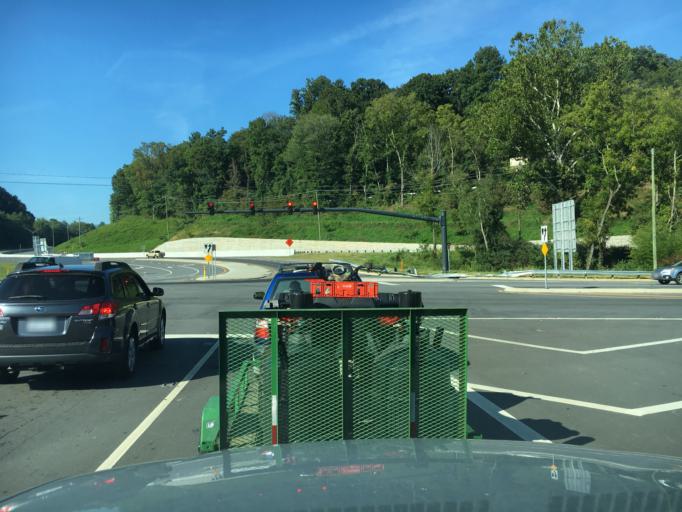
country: US
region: North Carolina
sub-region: Haywood County
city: Lake Junaluska
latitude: 35.5248
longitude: -82.9578
